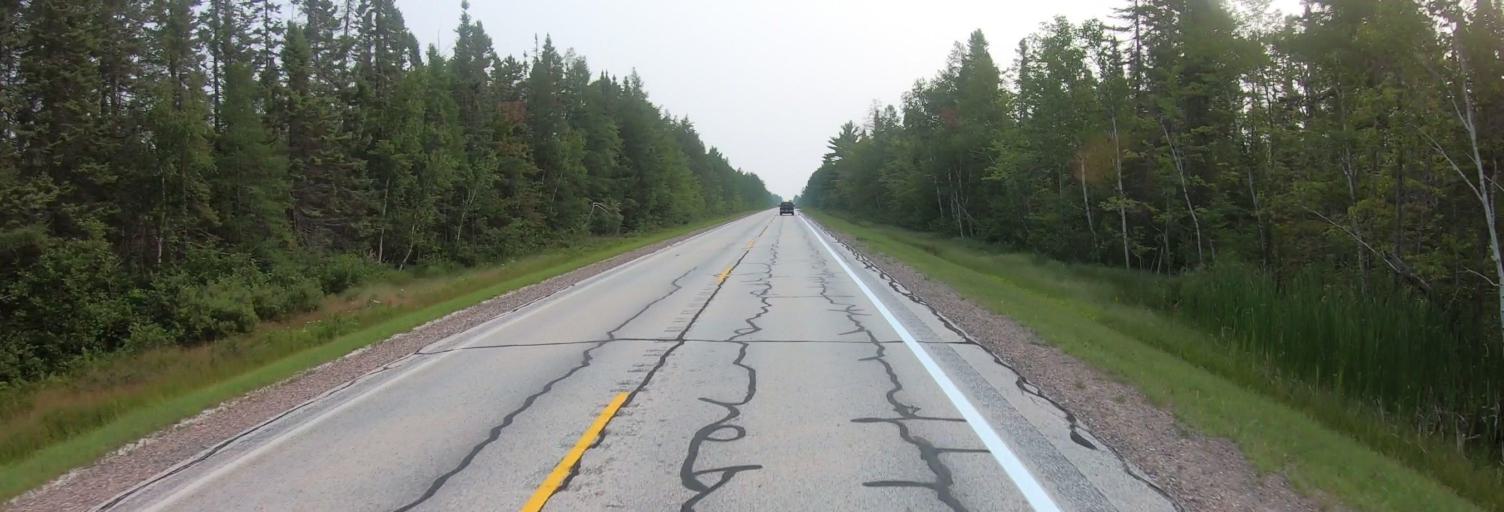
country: US
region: Michigan
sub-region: Luce County
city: Newberry
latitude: 46.5470
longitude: -85.0418
